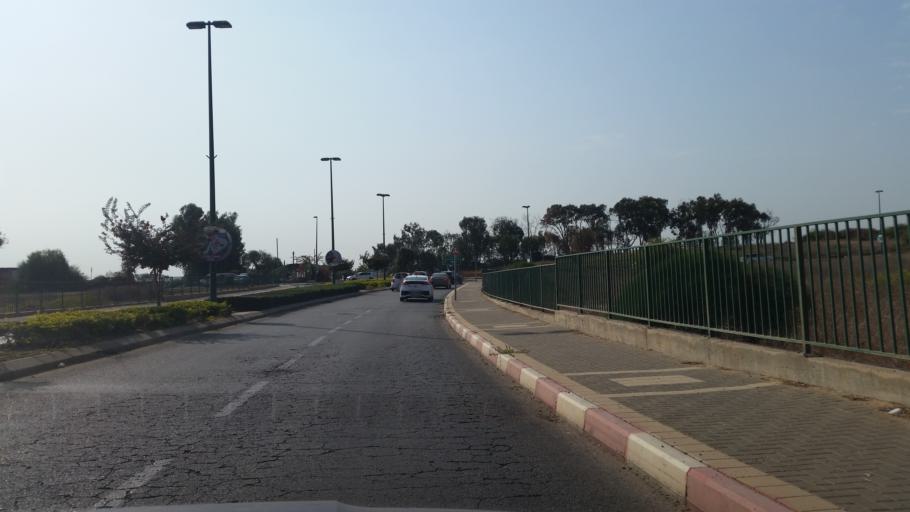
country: IL
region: Central District
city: Netanya
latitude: 32.3094
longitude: 34.8612
